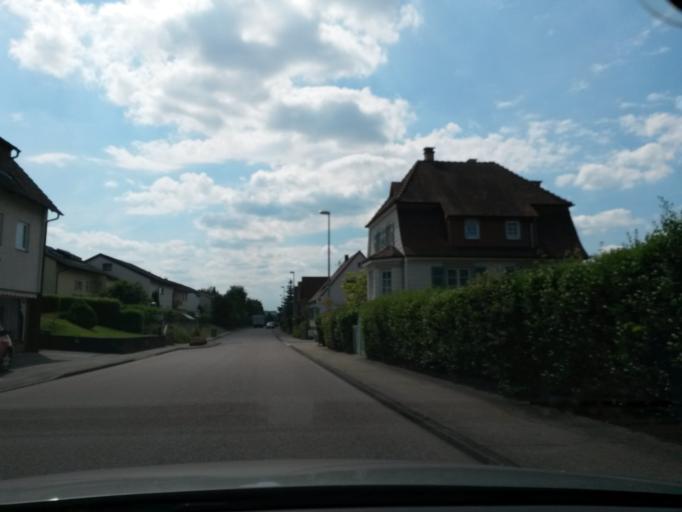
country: DE
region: Baden-Wuerttemberg
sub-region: Regierungsbezirk Stuttgart
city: Vaihingen an der Enz
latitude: 48.9541
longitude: 8.9786
